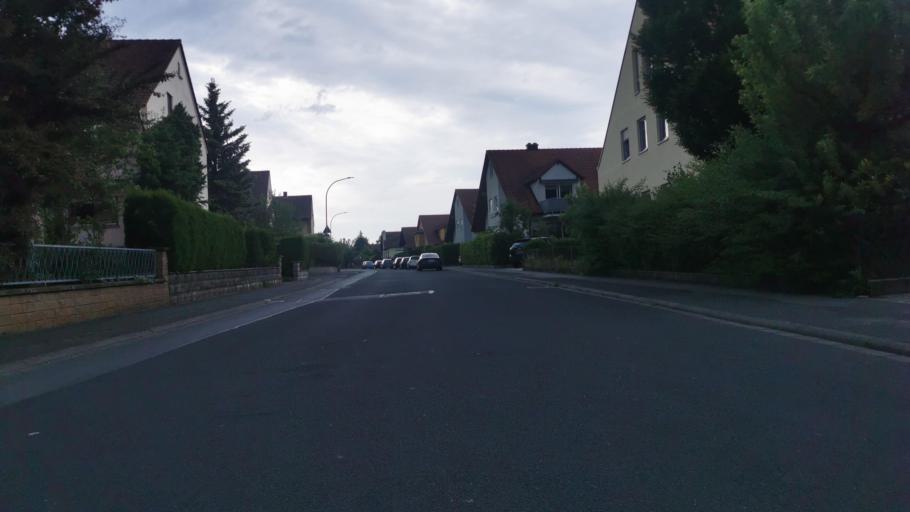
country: DE
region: Bavaria
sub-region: Regierungsbezirk Mittelfranken
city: Hochstadt an der Aisch
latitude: 49.7065
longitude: 10.8162
